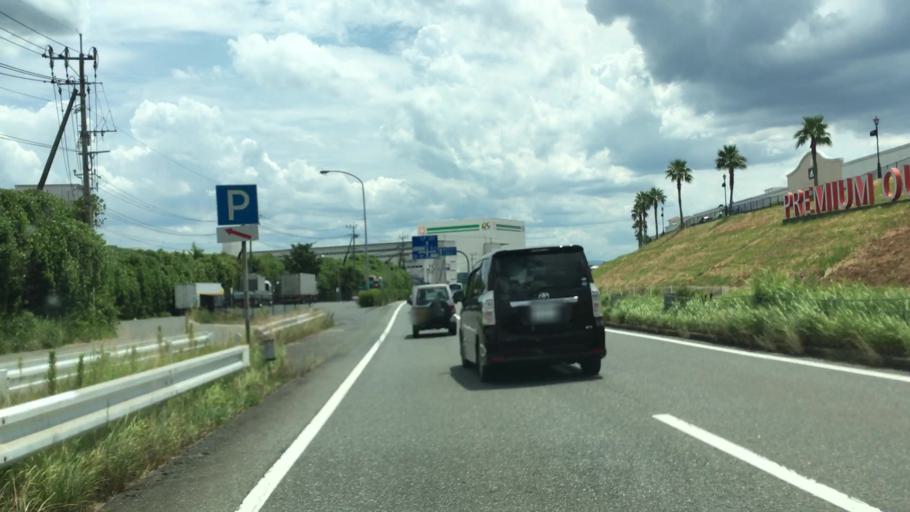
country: JP
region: Saga Prefecture
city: Tosu
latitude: 33.4072
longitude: 130.5126
